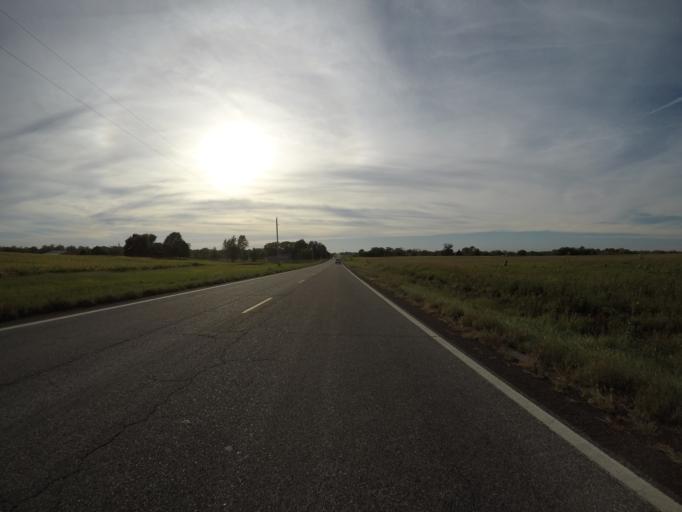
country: US
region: Kansas
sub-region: Douglas County
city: Baldwin City
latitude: 38.7823
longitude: -95.2105
